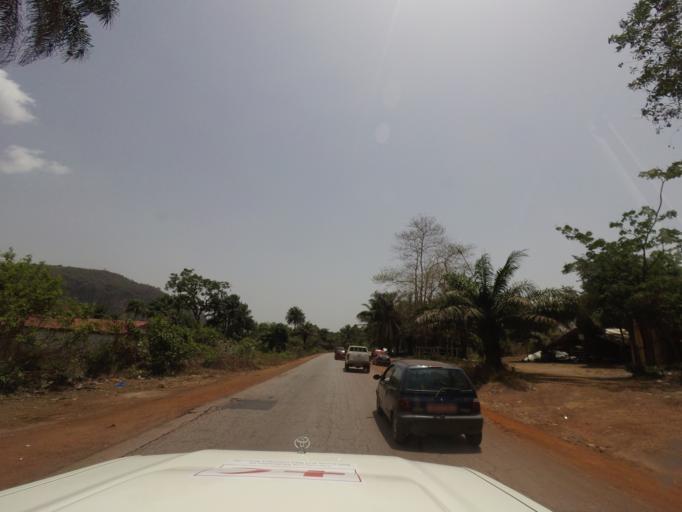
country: GN
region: Kindia
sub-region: Coyah
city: Coyah
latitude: 9.7797
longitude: -13.3418
